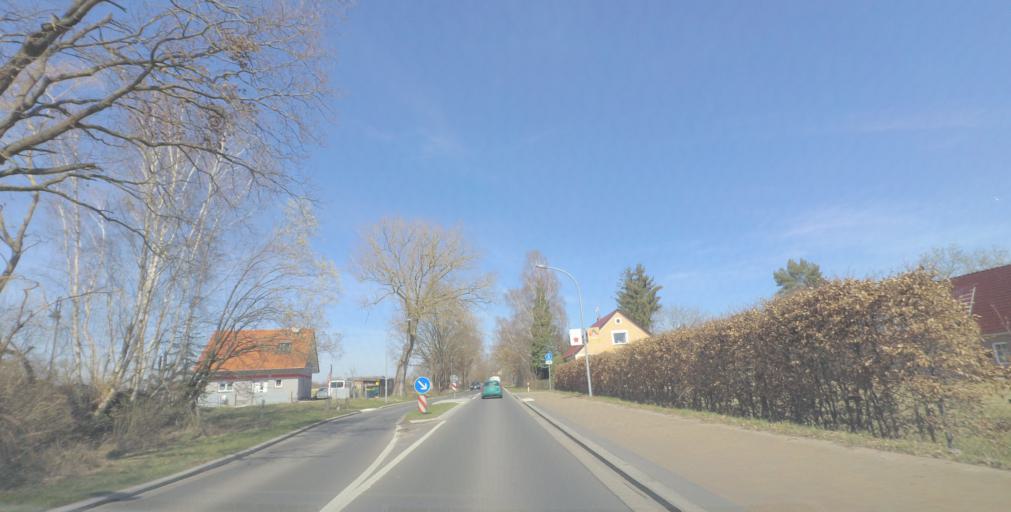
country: DE
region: Brandenburg
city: Neuruppin
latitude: 52.8973
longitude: 12.7992
